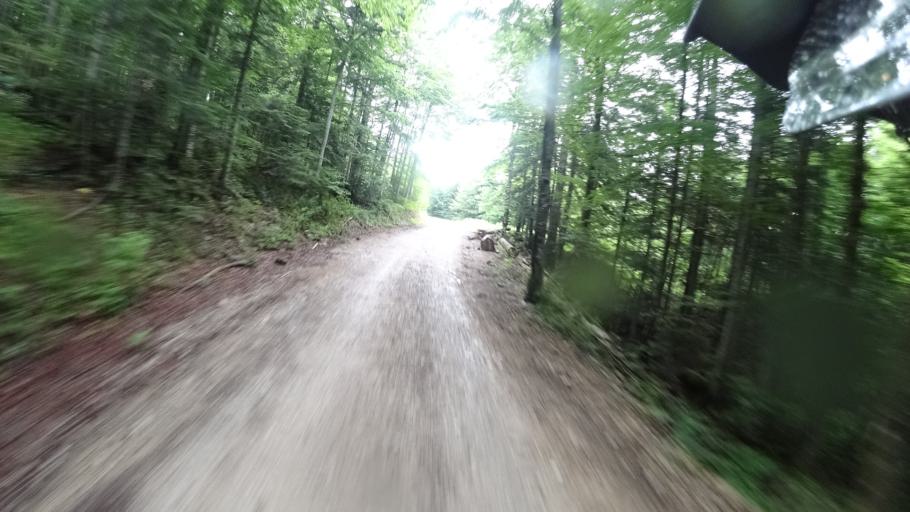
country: HR
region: Primorsko-Goranska
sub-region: Grad Delnice
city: Delnice
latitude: 45.3043
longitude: 14.9287
